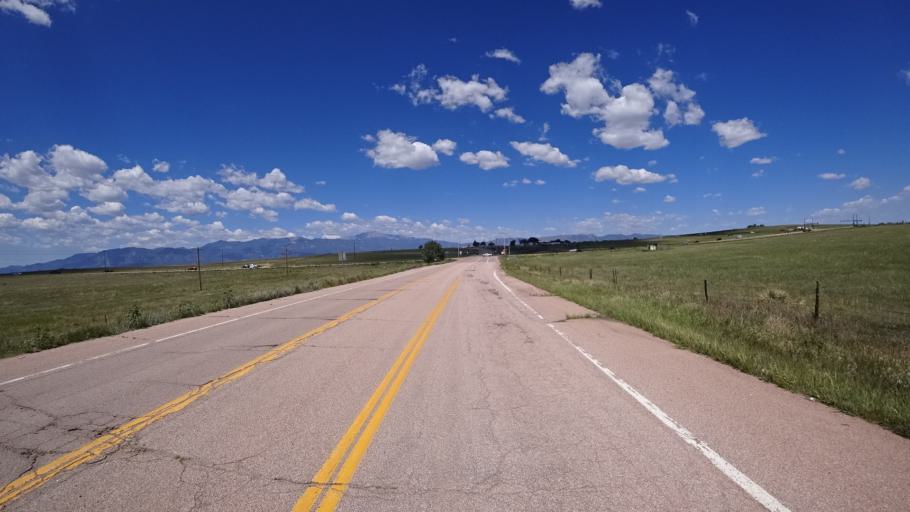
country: US
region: Colorado
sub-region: El Paso County
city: Cimarron Hills
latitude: 38.8376
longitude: -104.6805
